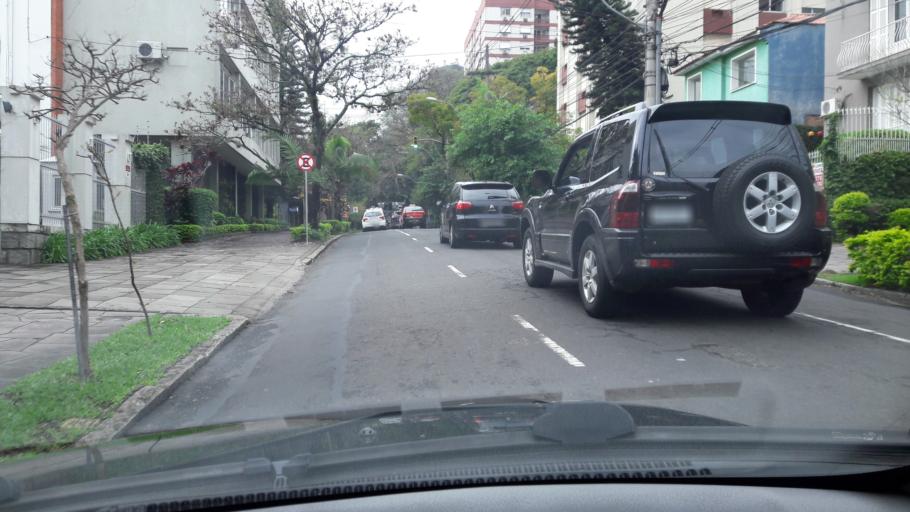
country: BR
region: Rio Grande do Sul
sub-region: Porto Alegre
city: Porto Alegre
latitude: -30.0284
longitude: -51.1978
